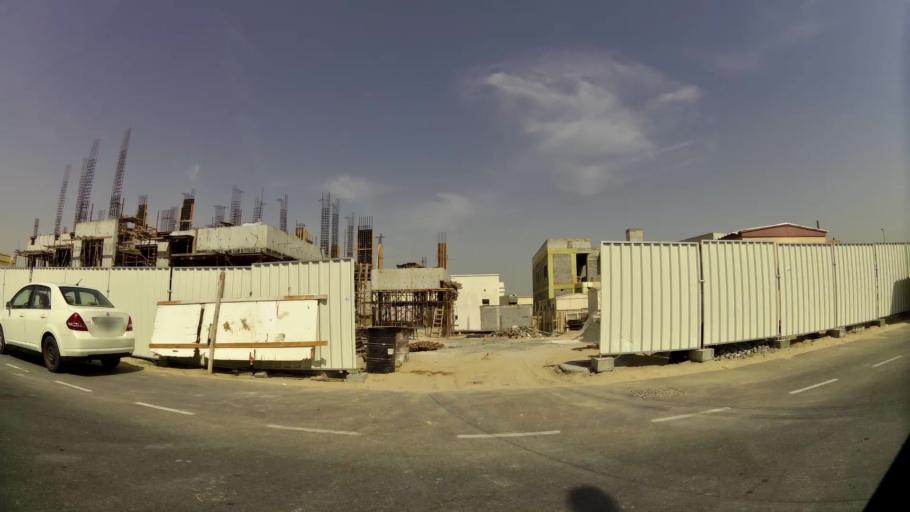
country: AE
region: Ash Shariqah
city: Sharjah
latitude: 25.2026
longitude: 55.4131
